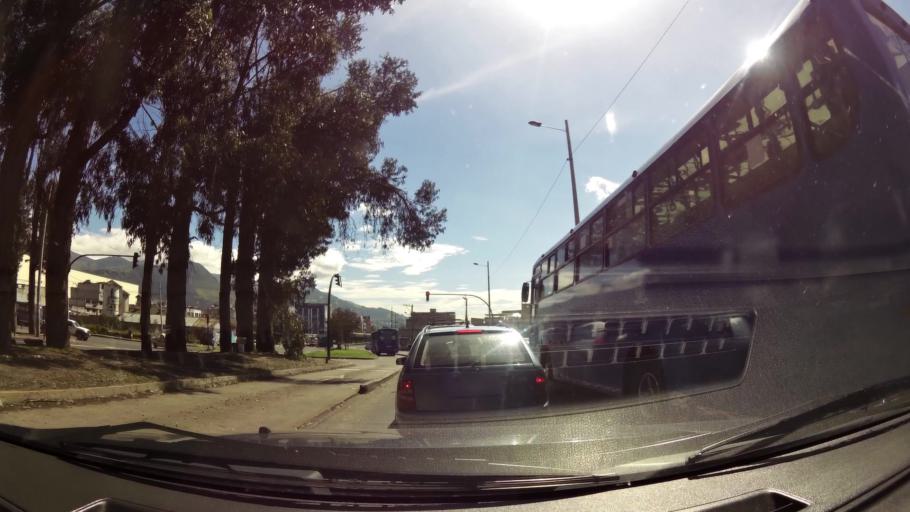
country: EC
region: Pichincha
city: Quito
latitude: -0.2835
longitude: -78.5546
